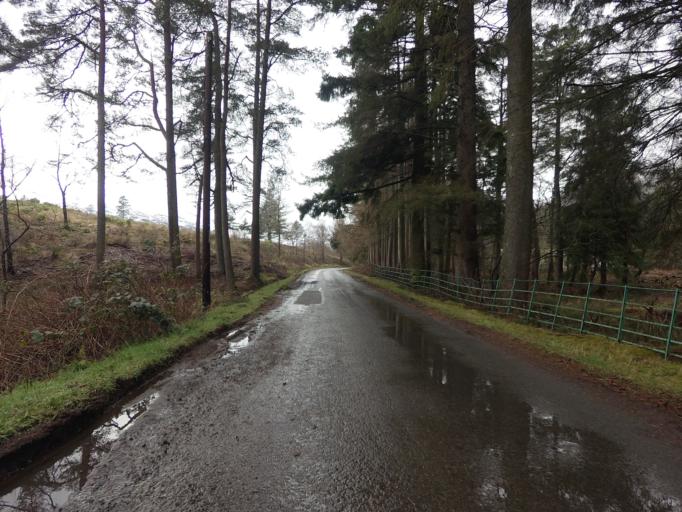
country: GB
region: Scotland
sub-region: West Dunbartonshire
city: Balloch
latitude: 56.2574
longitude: -4.5793
